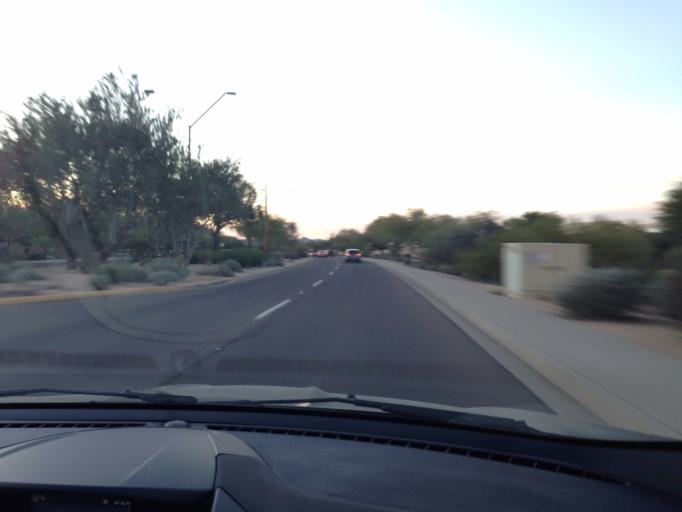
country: US
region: Arizona
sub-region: Maricopa County
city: Cave Creek
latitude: 33.7532
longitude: -111.9842
